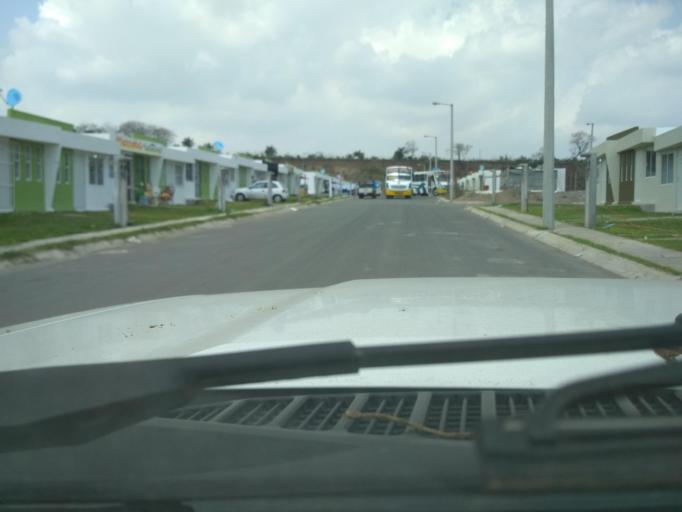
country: MX
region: Veracruz
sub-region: Veracruz
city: Lomas de Rio Medio Cuatro
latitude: 19.1853
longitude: -96.2139
